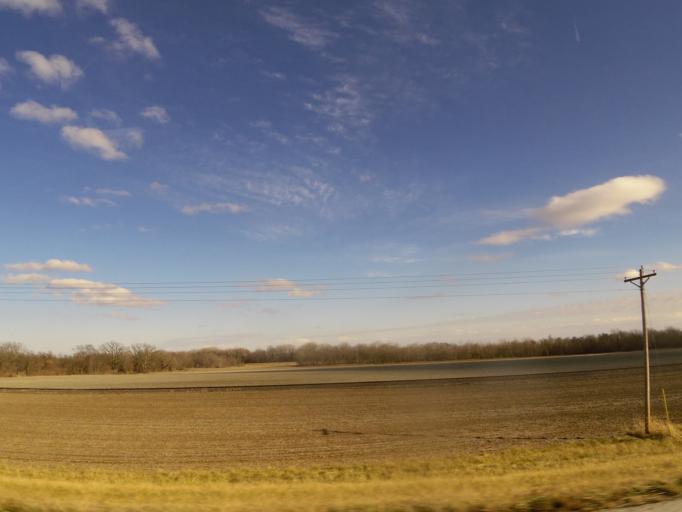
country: US
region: Missouri
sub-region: Lewis County
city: Canton
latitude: 40.1933
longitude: -91.5212
